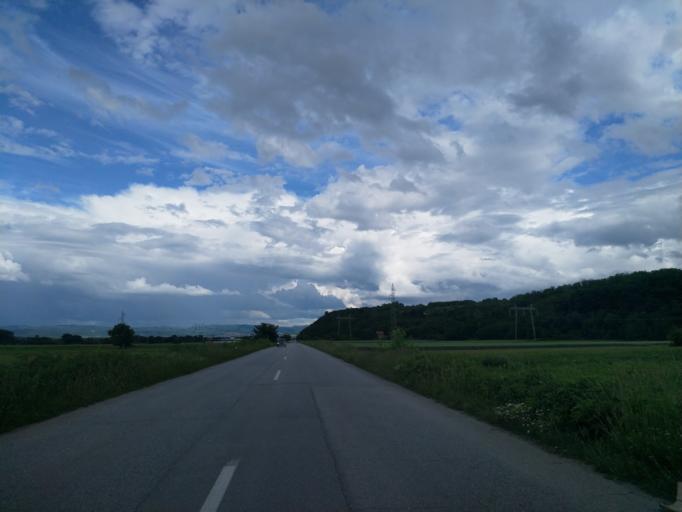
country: RS
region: Central Serbia
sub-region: Pomoravski Okrug
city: Jagodina
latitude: 43.9557
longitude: 21.3025
